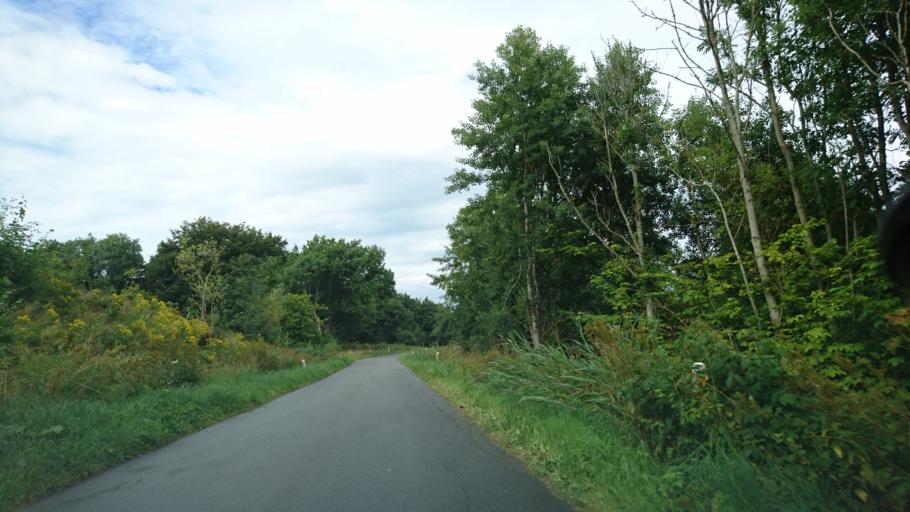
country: DK
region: North Denmark
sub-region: Frederikshavn Kommune
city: Frederikshavn
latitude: 57.4158
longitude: 10.4914
